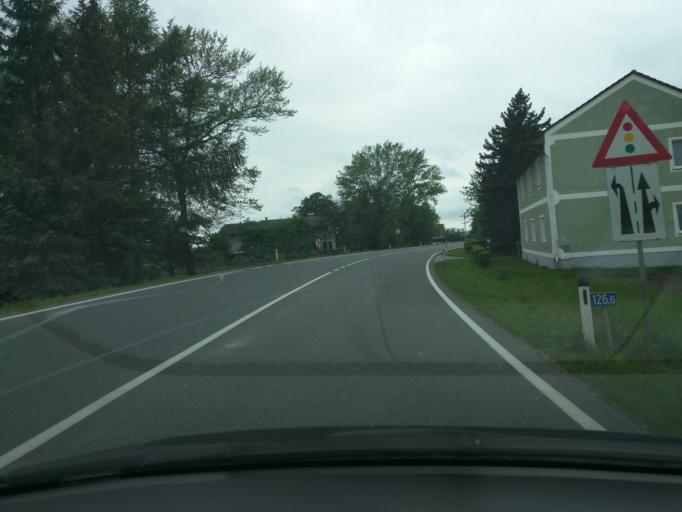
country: AT
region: Lower Austria
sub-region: Politischer Bezirk Amstetten
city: Sankt Georgen am Ybbsfelde
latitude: 48.1131
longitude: 14.9286
